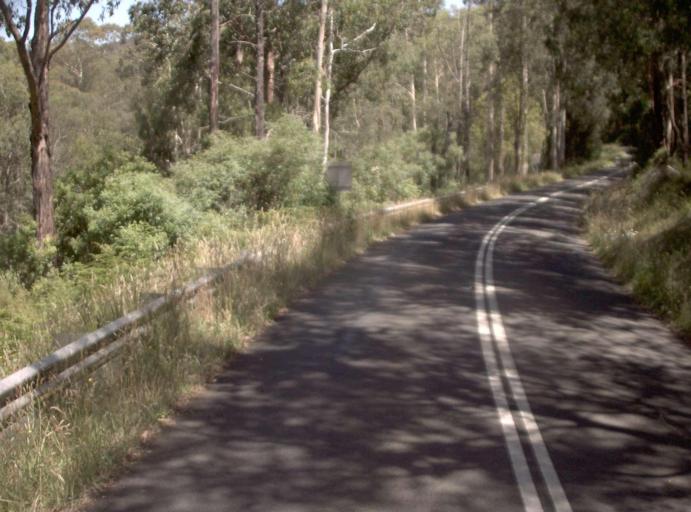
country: AU
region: Victoria
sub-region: Baw Baw
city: Warragul
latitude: -37.9012
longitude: 146.0128
